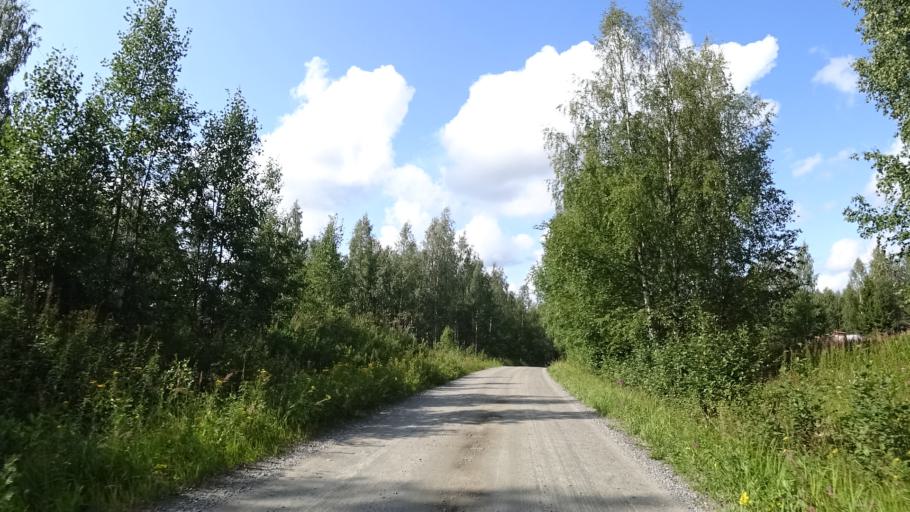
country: FI
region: North Karelia
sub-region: Joensuu
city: Ilomantsi
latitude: 62.9316
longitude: 31.3094
